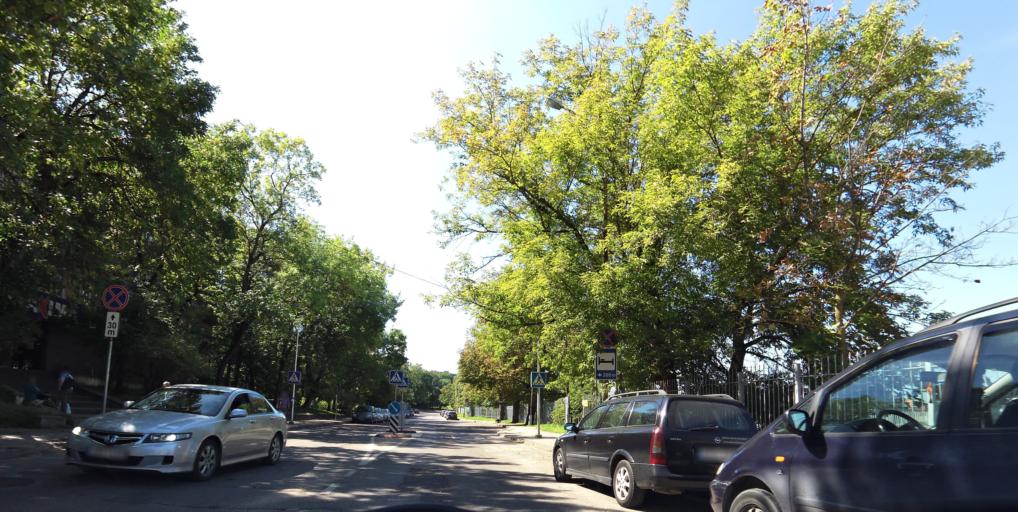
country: LT
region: Vilnius County
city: Naujamiestis
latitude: 54.6682
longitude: 25.2845
